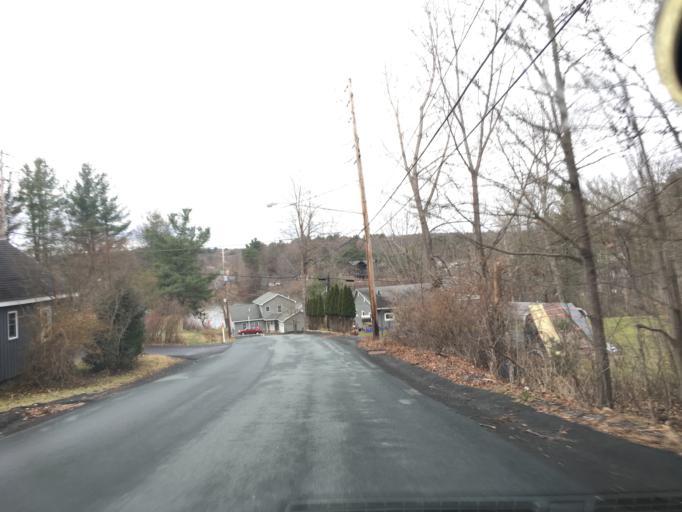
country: US
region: New York
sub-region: Rensselaer County
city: Averill Park
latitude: 42.6146
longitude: -73.5637
